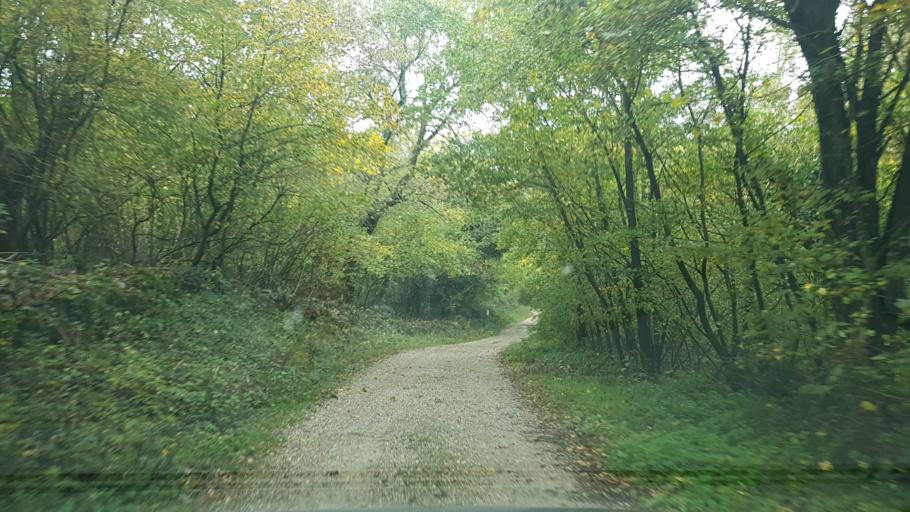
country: IT
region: Friuli Venezia Giulia
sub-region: Provincia di Gorizia
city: Monfalcone
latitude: 45.8173
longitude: 13.5295
